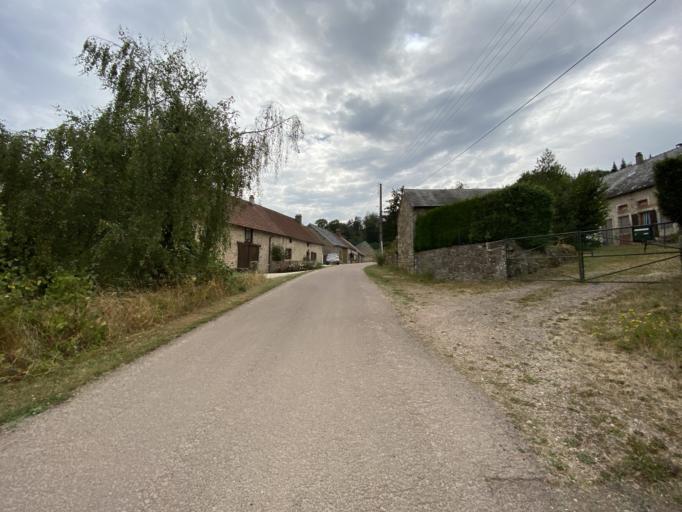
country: FR
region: Bourgogne
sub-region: Departement de la Cote-d'Or
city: Saulieu
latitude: 47.2582
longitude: 4.1353
